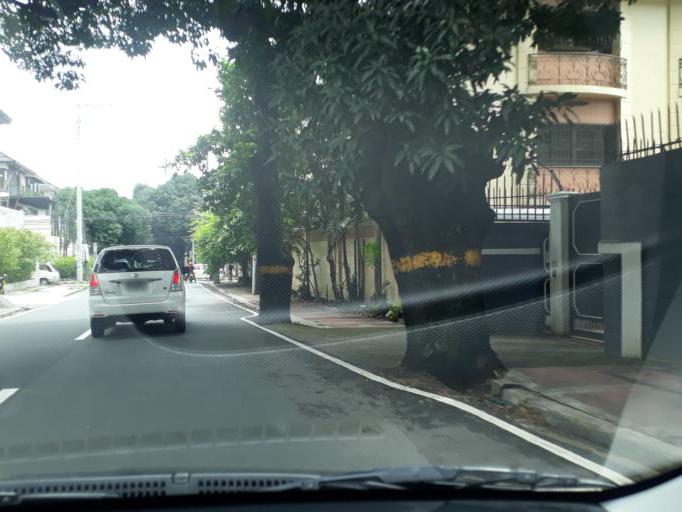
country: PH
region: Metro Manila
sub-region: San Juan
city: San Juan
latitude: 14.6223
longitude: 121.0295
